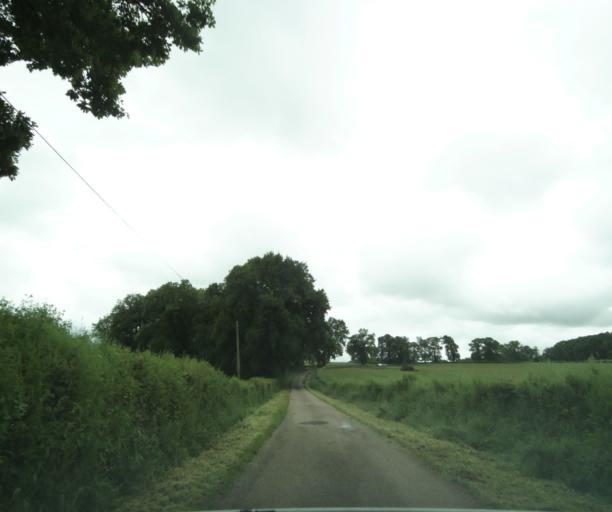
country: FR
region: Bourgogne
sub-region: Departement de Saone-et-Loire
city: Charolles
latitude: 46.4601
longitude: 4.2901
